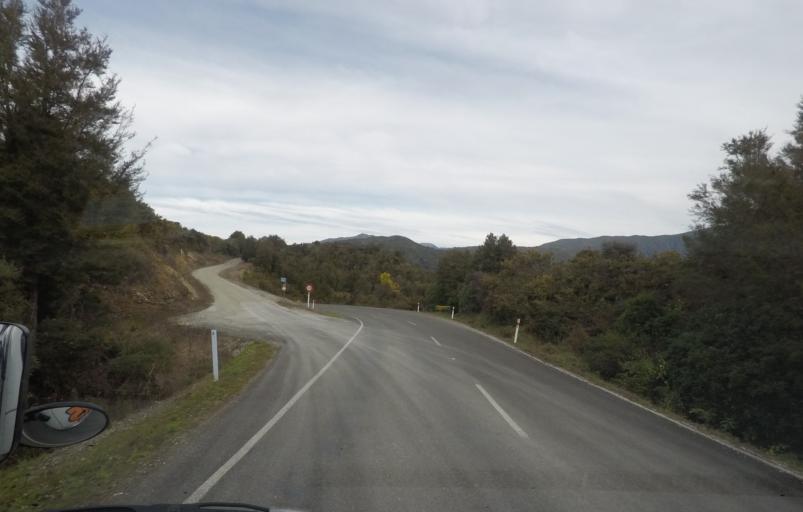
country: NZ
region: Tasman
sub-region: Tasman District
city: Takaka
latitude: -40.8464
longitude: 172.7731
